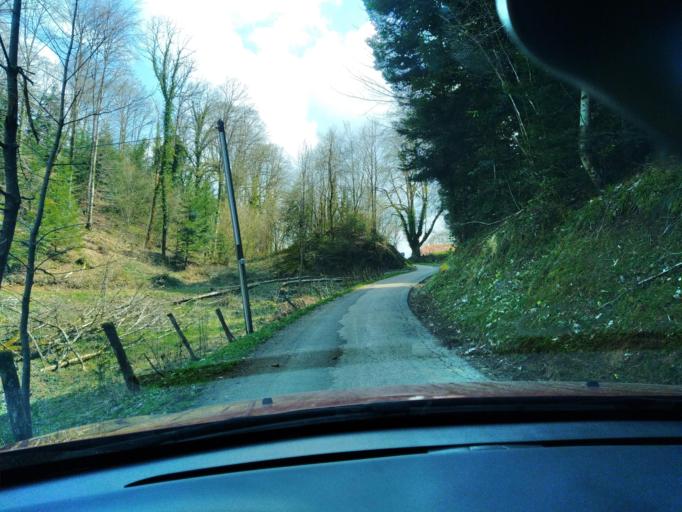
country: FR
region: Franche-Comte
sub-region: Departement du Jura
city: Lavans-les-Saint-Claude
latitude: 46.3966
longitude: 5.7550
